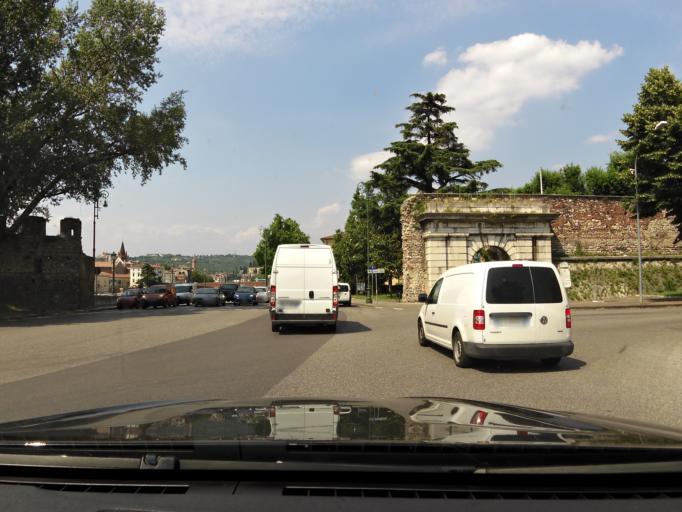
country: IT
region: Veneto
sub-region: Provincia di Verona
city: Verona
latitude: 45.4354
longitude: 11.0015
